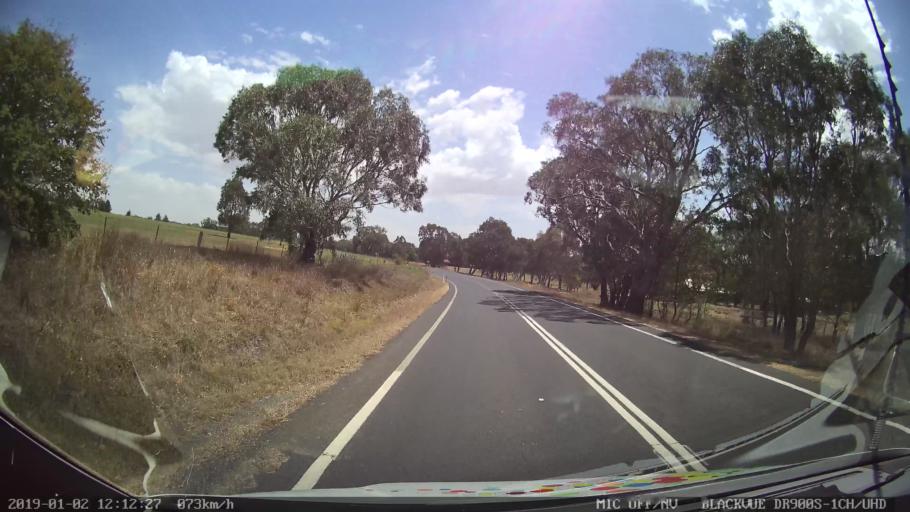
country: AU
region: New South Wales
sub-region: Young
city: Young
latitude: -34.4369
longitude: 148.2548
